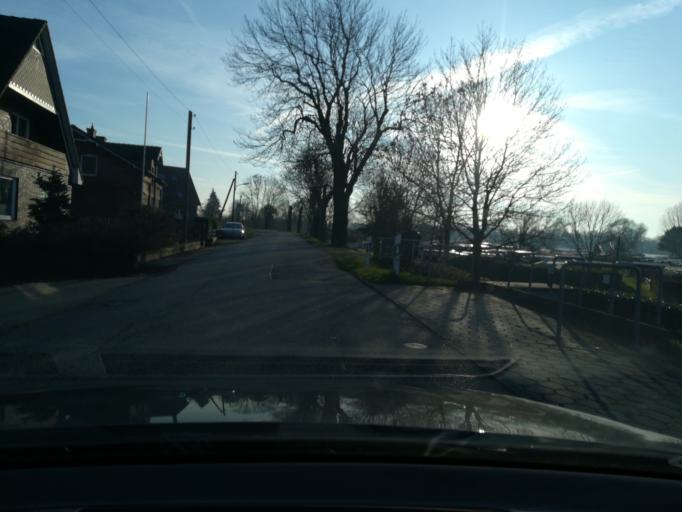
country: DE
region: Lower Saxony
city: Stelle
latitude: 53.4424
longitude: 10.1114
